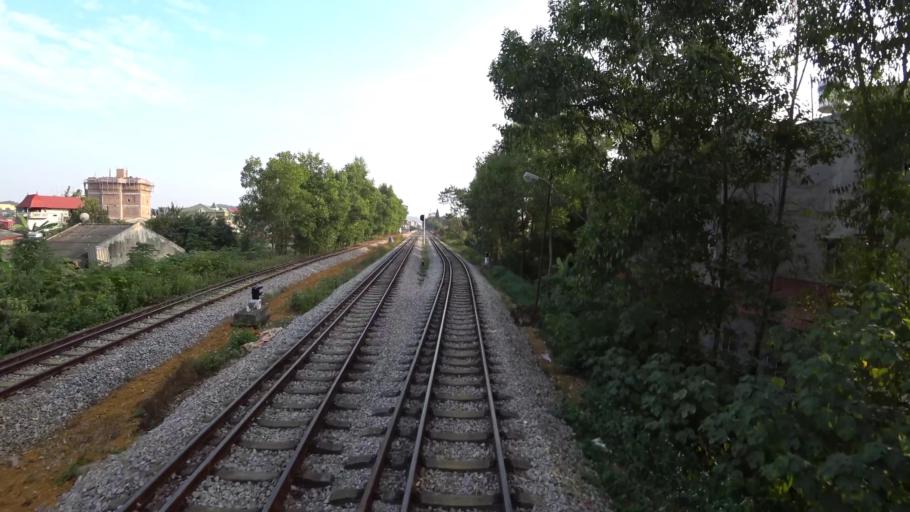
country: VN
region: Lang Son
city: Thi Tran Cao Loc
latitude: 21.8704
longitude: 106.7606
